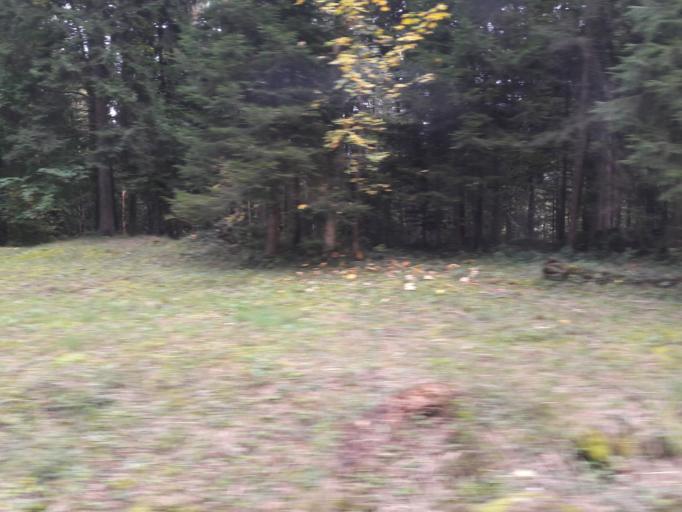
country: CH
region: Schwyz
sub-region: Bezirk Schwyz
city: Goldau
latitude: 47.0531
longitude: 8.5680
